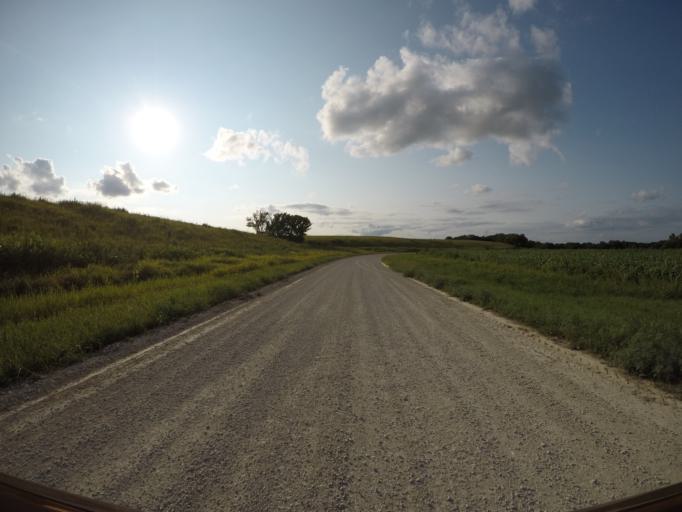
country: US
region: Kansas
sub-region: Wabaunsee County
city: Alma
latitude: 38.8809
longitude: -96.2068
